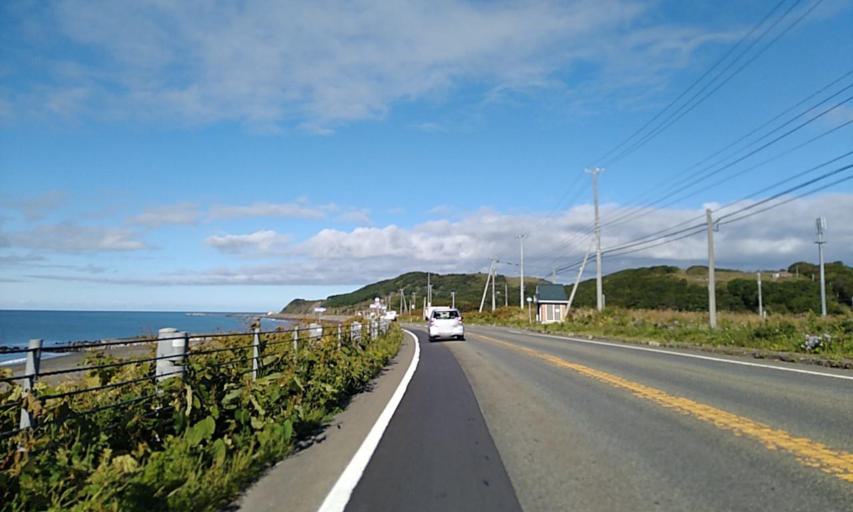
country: JP
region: Hokkaido
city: Shizunai-furukawacho
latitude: 42.1854
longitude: 142.7223
